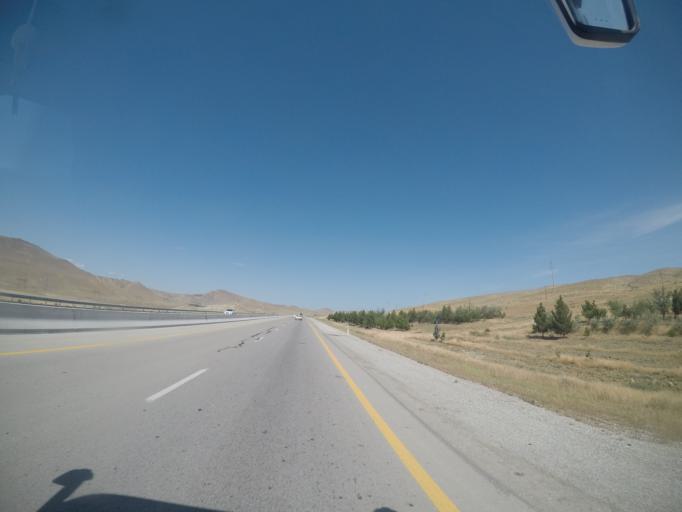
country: AZ
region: Sumqayit
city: Haci Zeynalabdin
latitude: 40.5007
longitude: 49.2843
